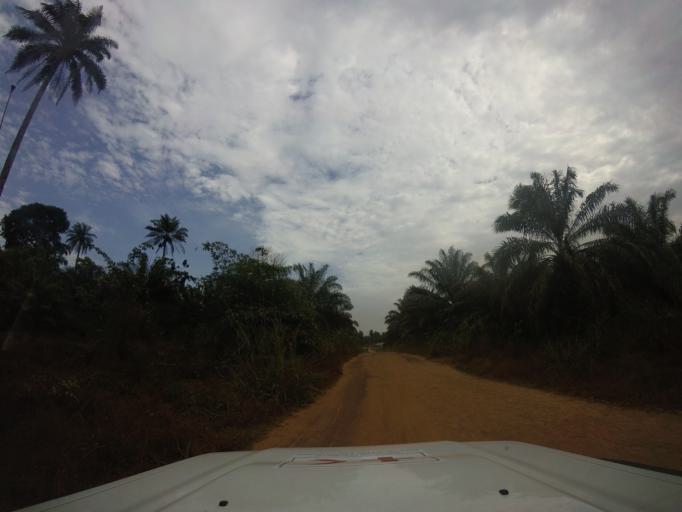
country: LR
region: Grand Cape Mount
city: Robertsport
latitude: 7.0215
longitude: -11.2888
